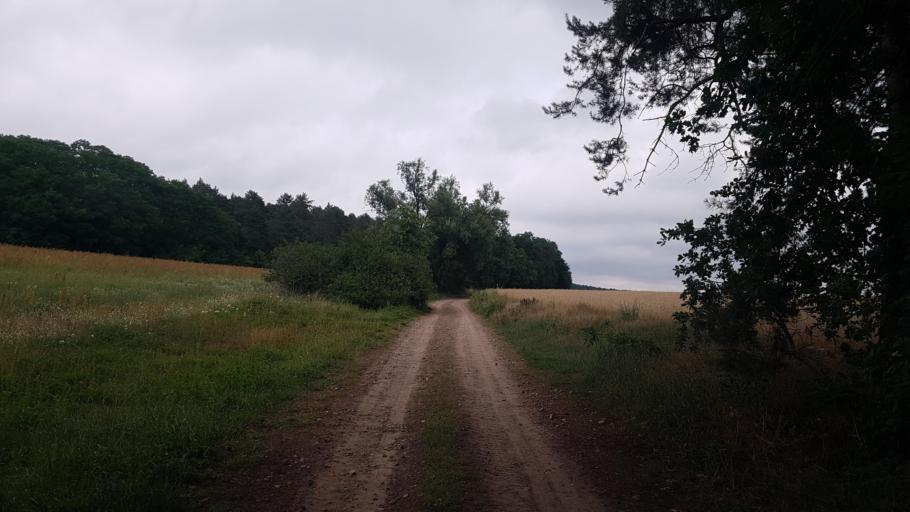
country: DE
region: Brandenburg
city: Trebbin
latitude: 52.2424
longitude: 13.1692
